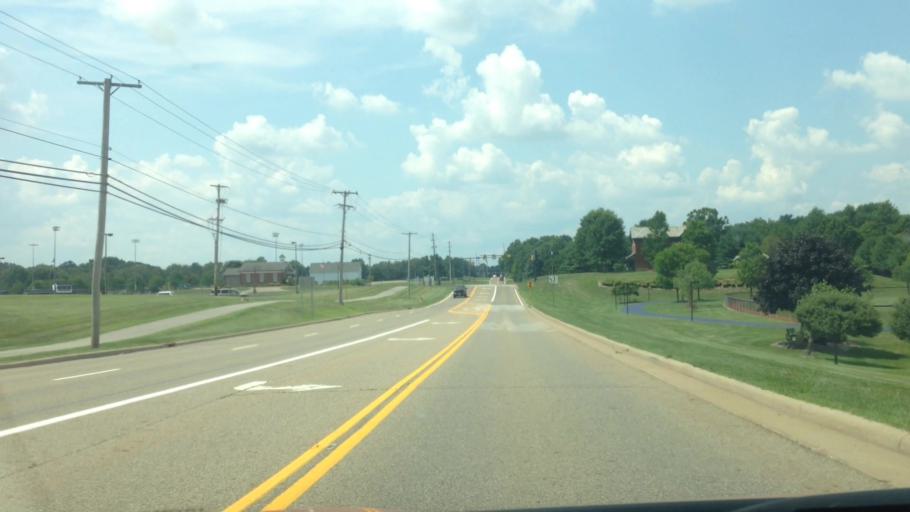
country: US
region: Ohio
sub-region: Stark County
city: Perry Heights
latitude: 40.8609
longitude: -81.4909
